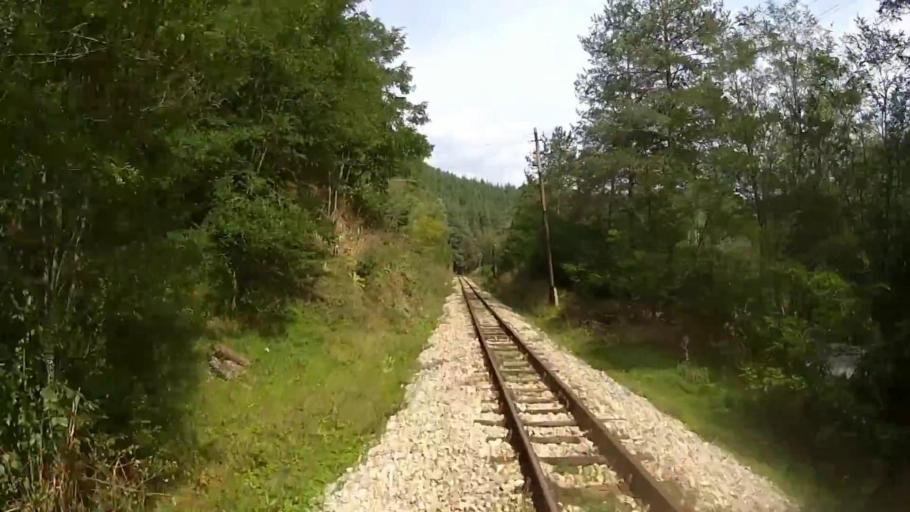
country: BG
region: Blagoevgrad
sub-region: Obshtina Yakoruda
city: Yakoruda
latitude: 42.0350
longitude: 23.7805
